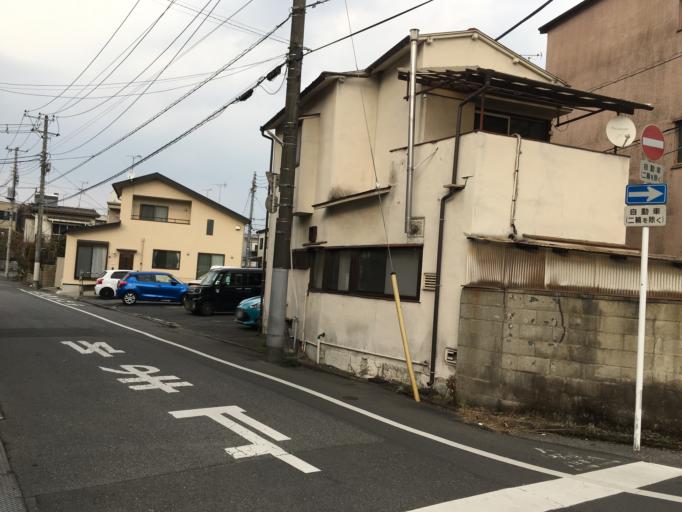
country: JP
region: Tochigi
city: Utsunomiya-shi
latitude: 36.5622
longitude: 139.8918
